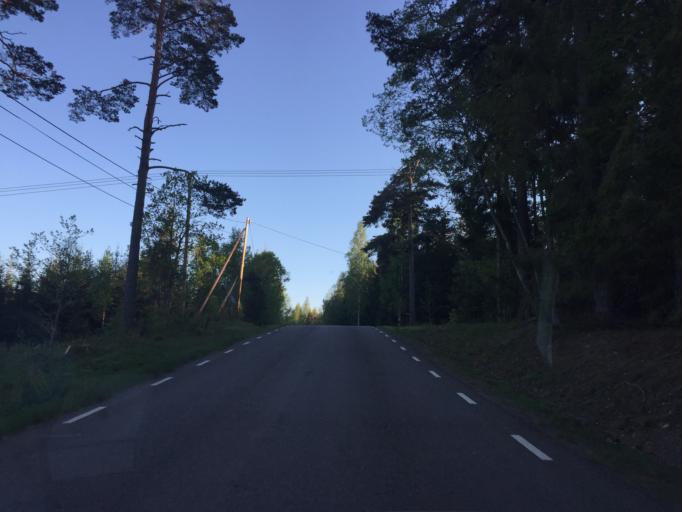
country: SE
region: Soedermanland
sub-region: Vingakers Kommun
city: Vingaker
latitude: 59.0112
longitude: 15.6760
